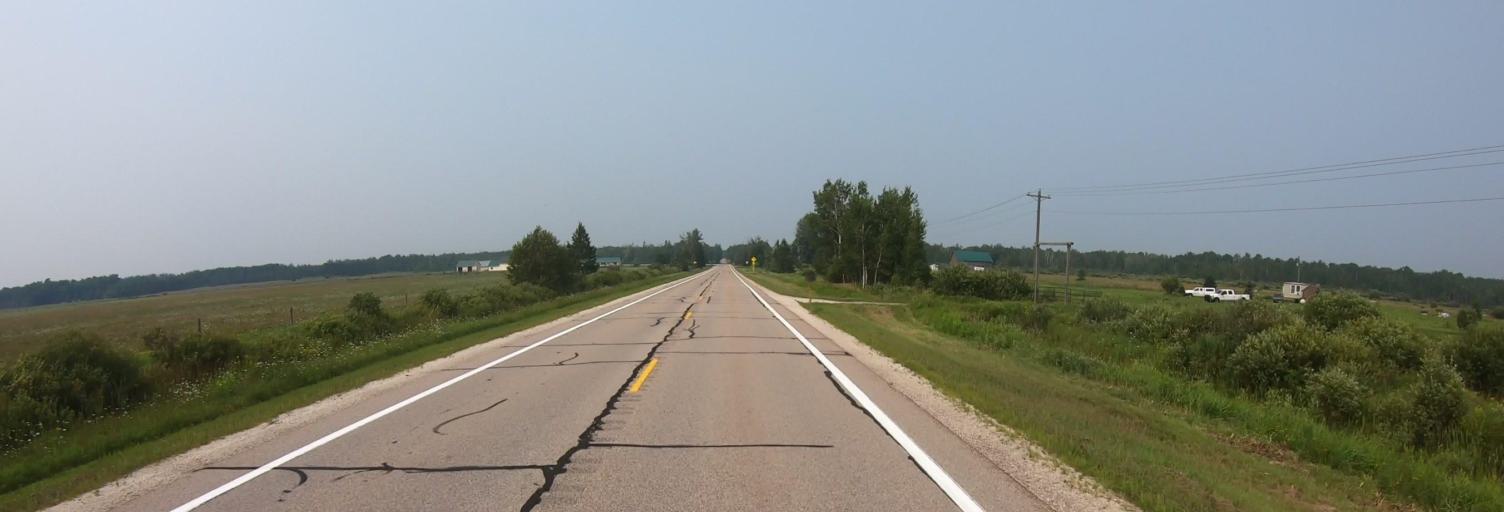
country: US
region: Michigan
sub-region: Chippewa County
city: Sault Ste. Marie
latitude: 46.1220
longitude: -84.2595
